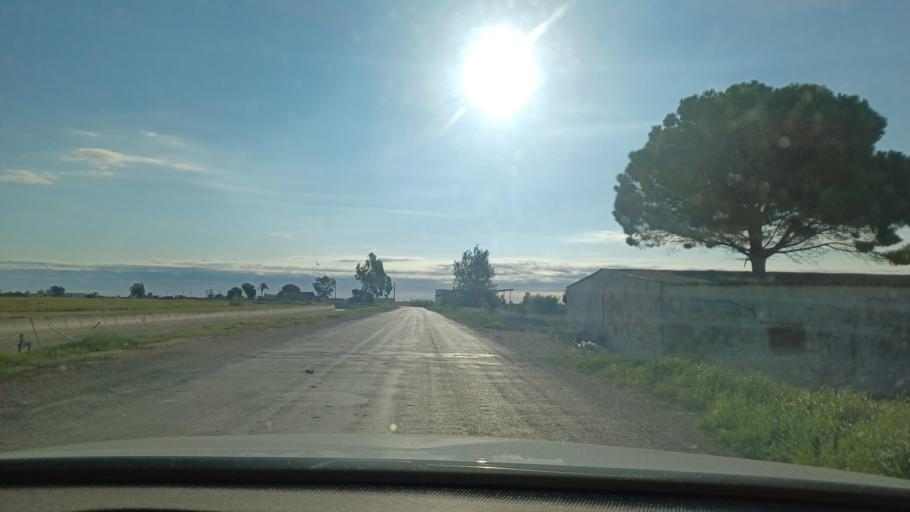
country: ES
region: Catalonia
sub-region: Provincia de Tarragona
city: Amposta
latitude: 40.6993
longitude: 0.6117
